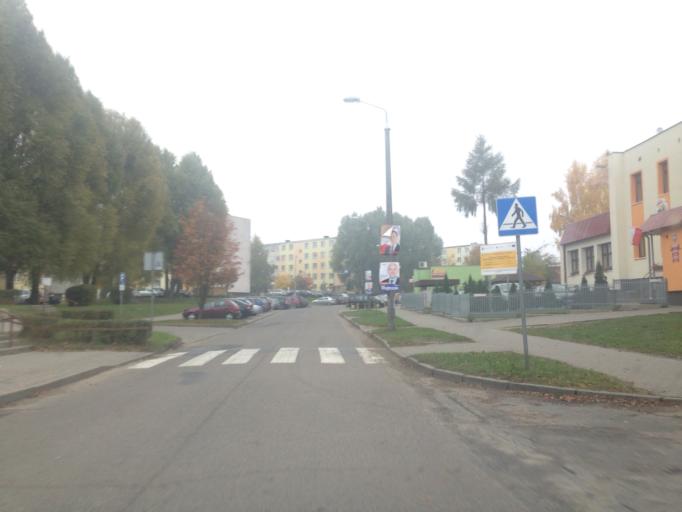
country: PL
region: Kujawsko-Pomorskie
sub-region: Powiat brodnicki
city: Brodnica
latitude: 53.2462
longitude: 19.4090
